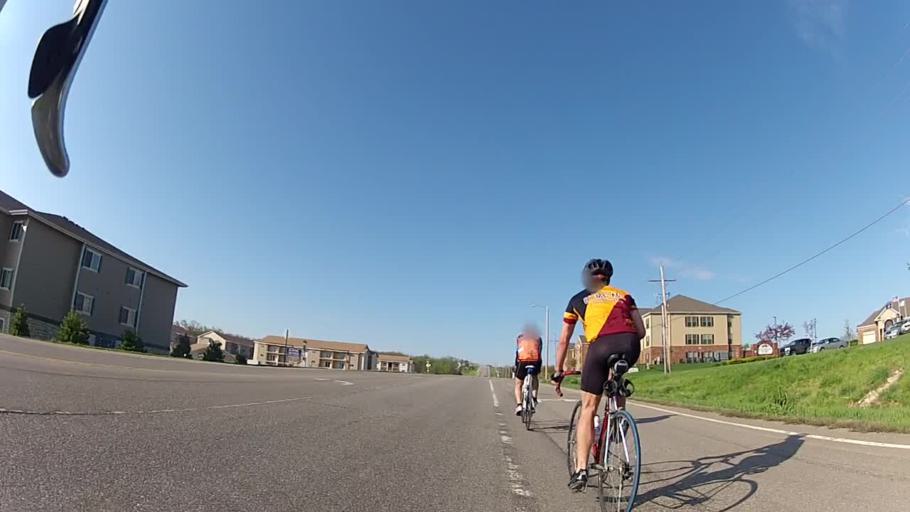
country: US
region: Kansas
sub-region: Riley County
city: Manhattan
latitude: 39.1857
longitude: -96.6434
